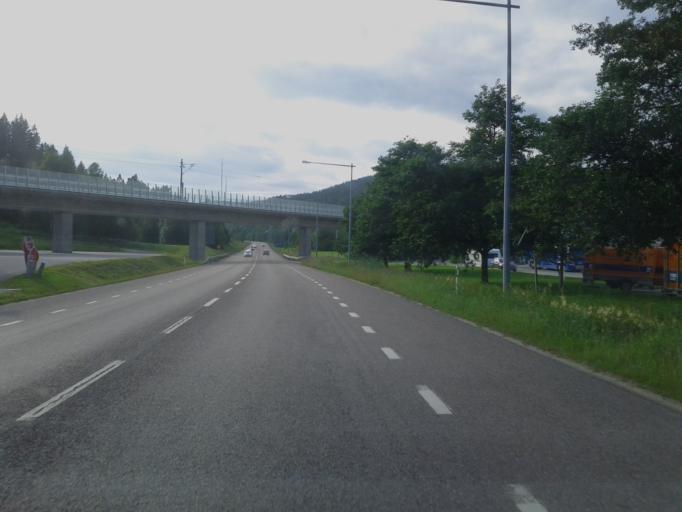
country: SE
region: Vaesternorrland
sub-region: OErnskoeldsviks Kommun
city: Ornskoldsvik
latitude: 63.2914
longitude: 18.7047
